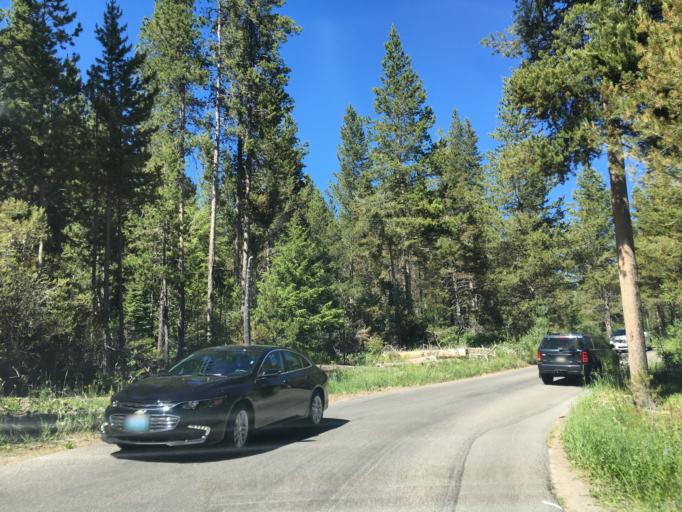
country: US
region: Wyoming
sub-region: Teton County
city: Moose Wilson Road
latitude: 43.6274
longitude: -110.7818
